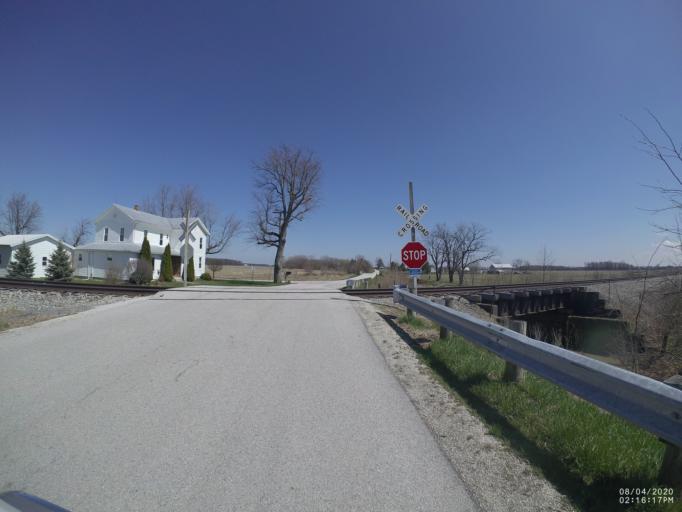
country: US
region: Ohio
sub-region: Sandusky County
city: Gibsonburg
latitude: 41.2826
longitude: -83.2591
